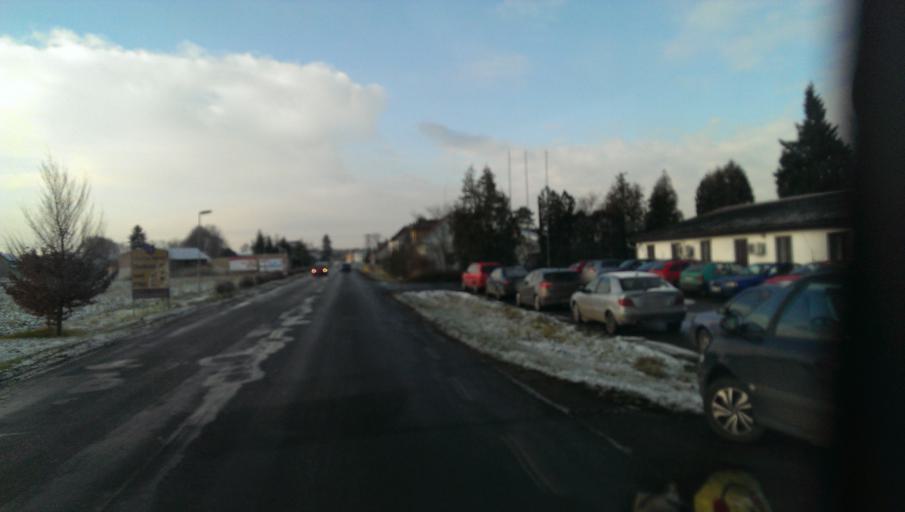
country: CZ
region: Ustecky
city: Budyne nad Ohri
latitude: 50.4063
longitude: 14.1382
